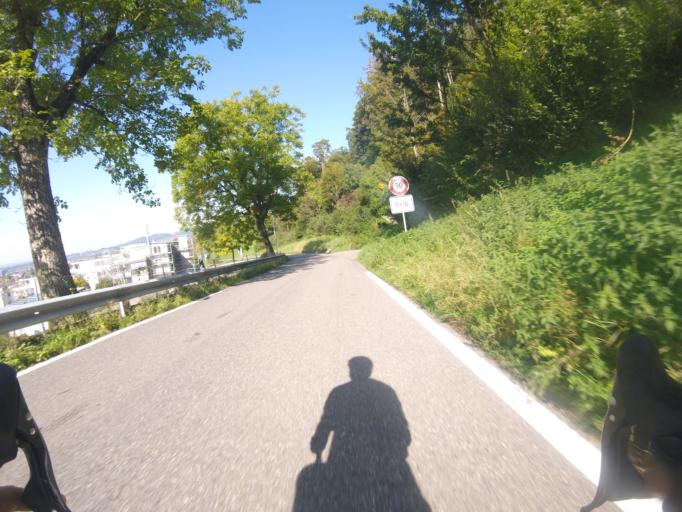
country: CH
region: Bern
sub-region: Bern-Mittelland District
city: Belp
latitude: 46.8801
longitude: 7.5081
